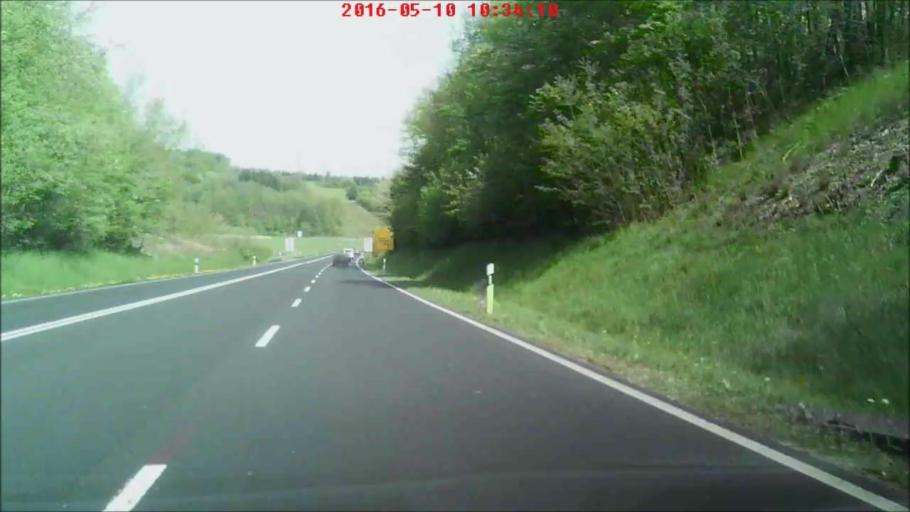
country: DE
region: Hesse
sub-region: Regierungsbezirk Kassel
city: Petersberg
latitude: 50.6178
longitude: 9.7303
